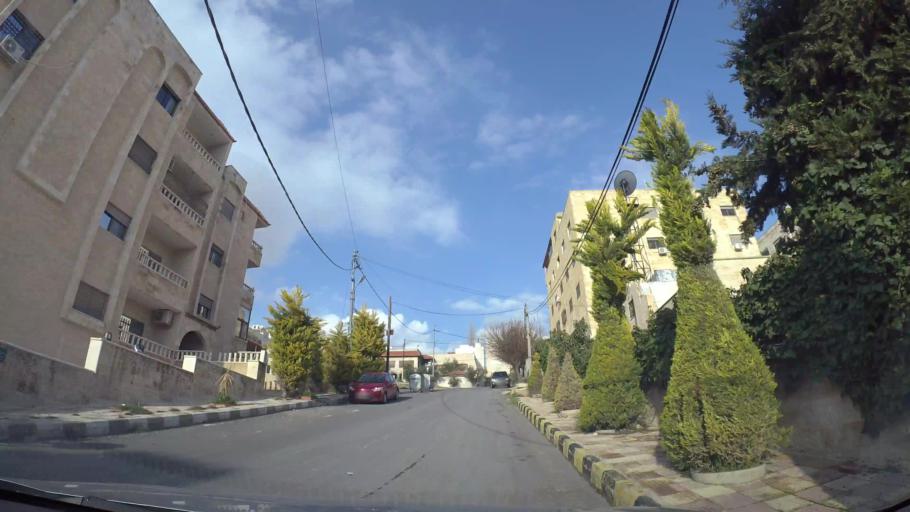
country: JO
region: Amman
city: Al Jubayhah
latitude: 32.0072
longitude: 35.8633
